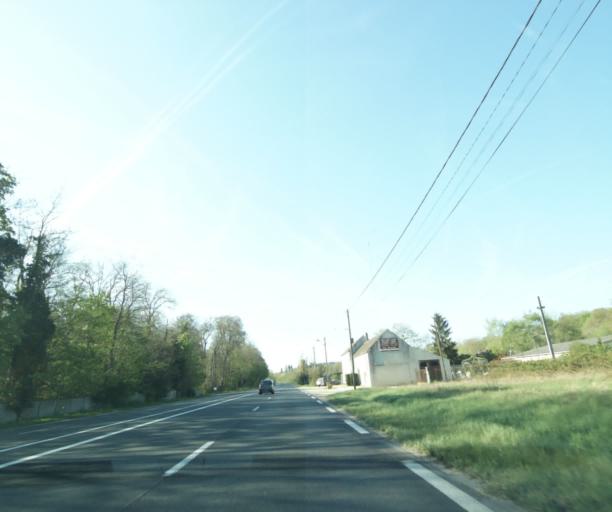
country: FR
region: Ile-de-France
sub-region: Departement de Seine-et-Marne
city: Grez-sur-Loing
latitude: 48.3028
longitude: 2.6799
